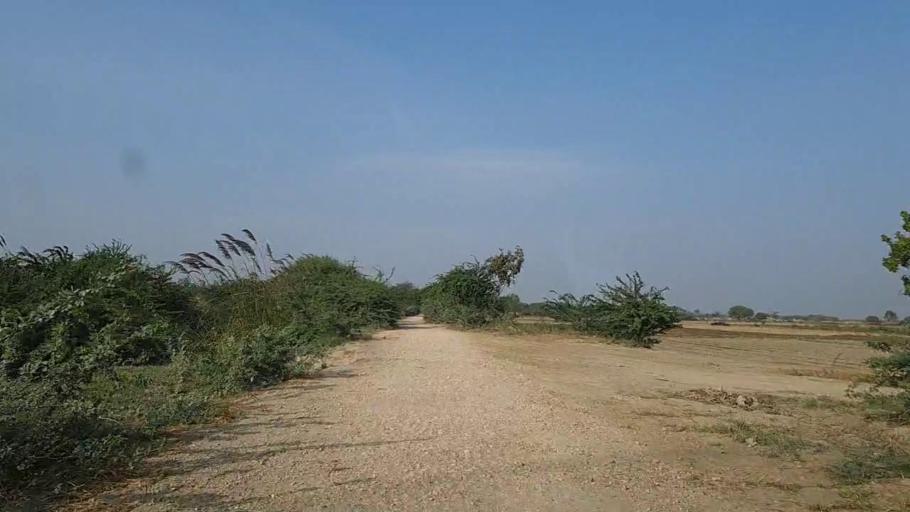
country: PK
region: Sindh
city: Mirpur Sakro
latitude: 24.5963
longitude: 67.6488
